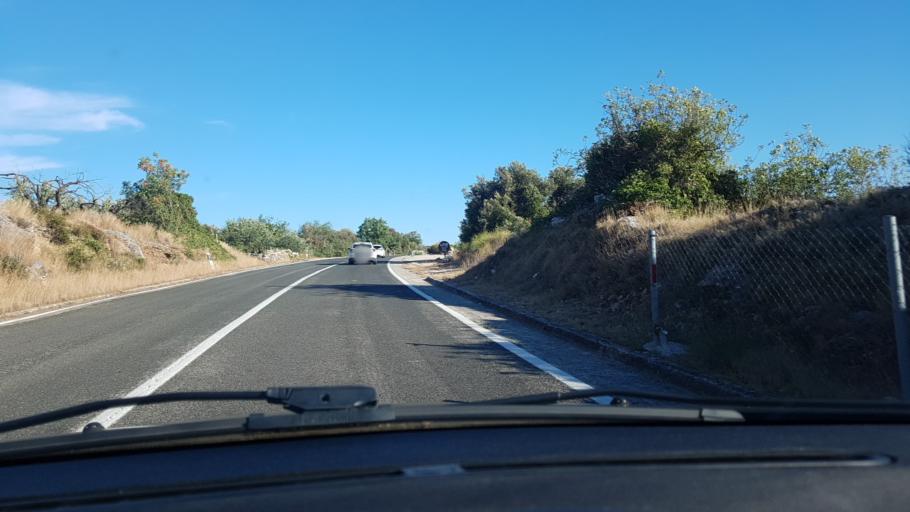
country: HR
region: Sibensko-Kniniska
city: Primosten
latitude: 43.5797
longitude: 15.9379
